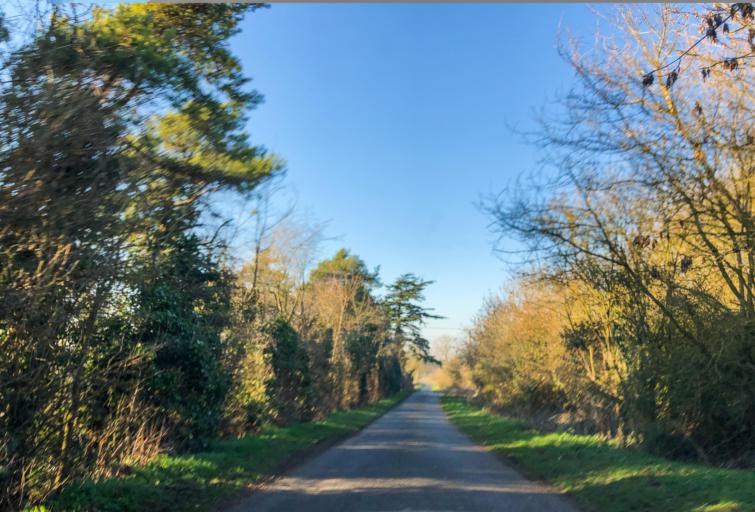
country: GB
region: England
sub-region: Warwickshire
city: Warwick
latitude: 52.2437
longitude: -1.5863
